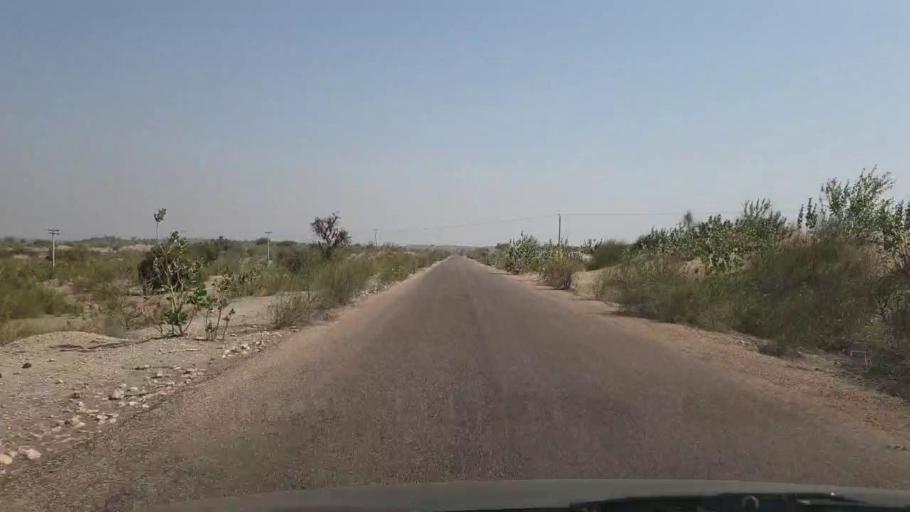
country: PK
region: Sindh
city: Chor
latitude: 25.6017
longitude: 70.0207
